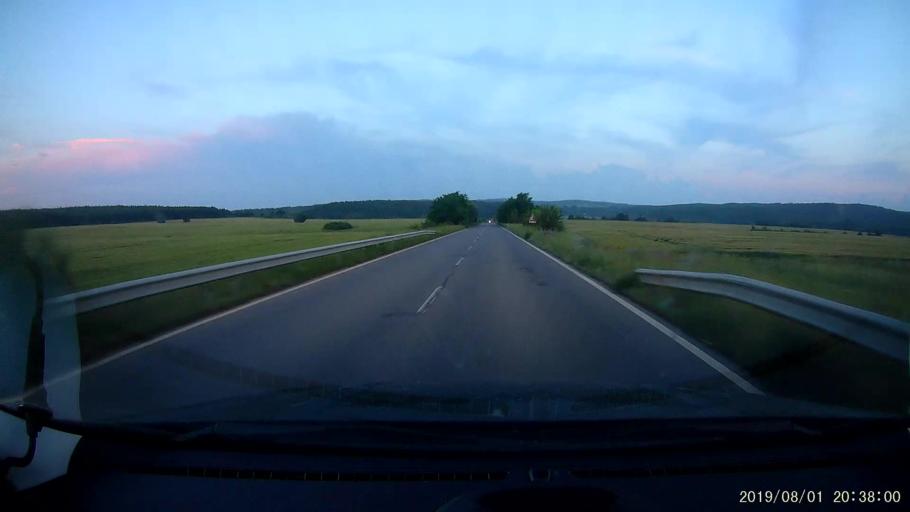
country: BG
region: Yambol
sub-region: Obshtina Elkhovo
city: Elkhovo
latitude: 42.0358
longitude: 26.5973
